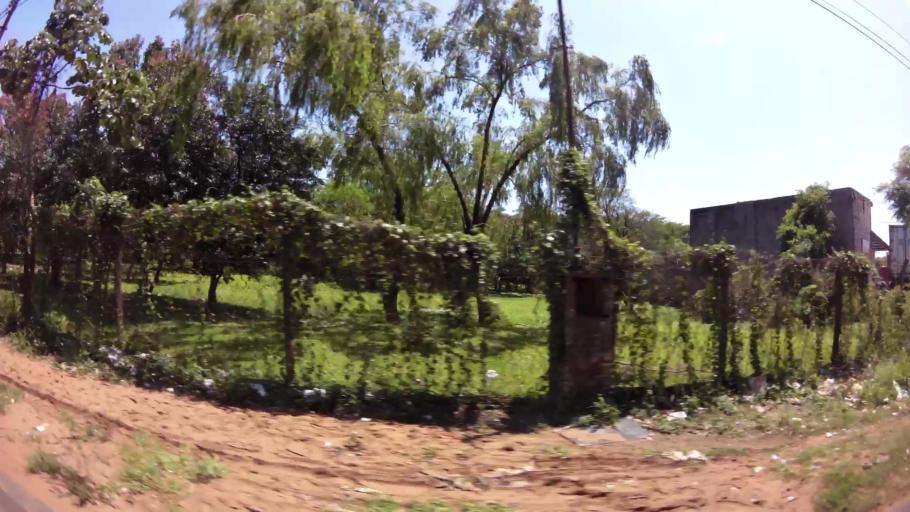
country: PY
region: Central
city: Nemby
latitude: -25.3973
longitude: -57.5317
